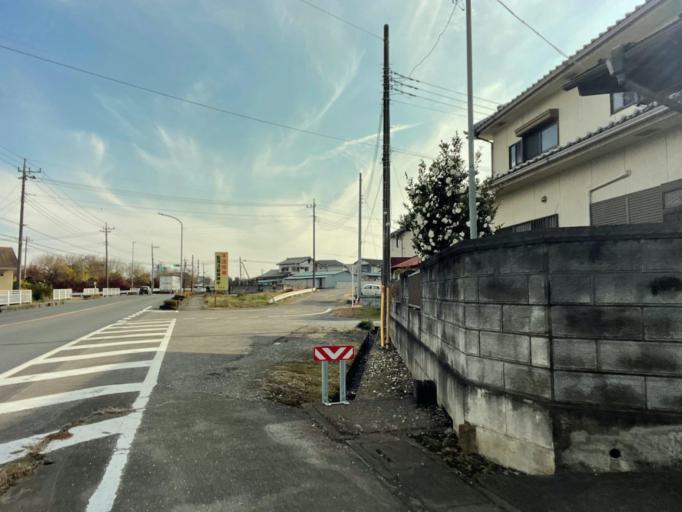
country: JP
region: Saitama
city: Yorii
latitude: 36.1471
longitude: 139.1944
